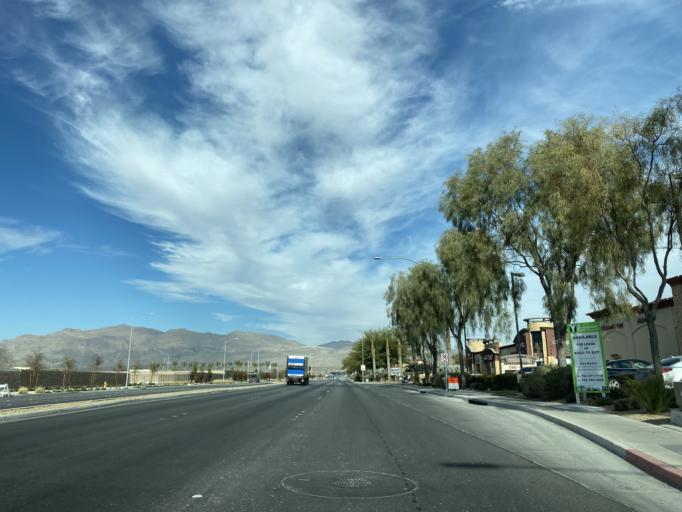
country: US
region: Nevada
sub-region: Clark County
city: Nellis Air Force Base
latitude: 36.2765
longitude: -115.1168
